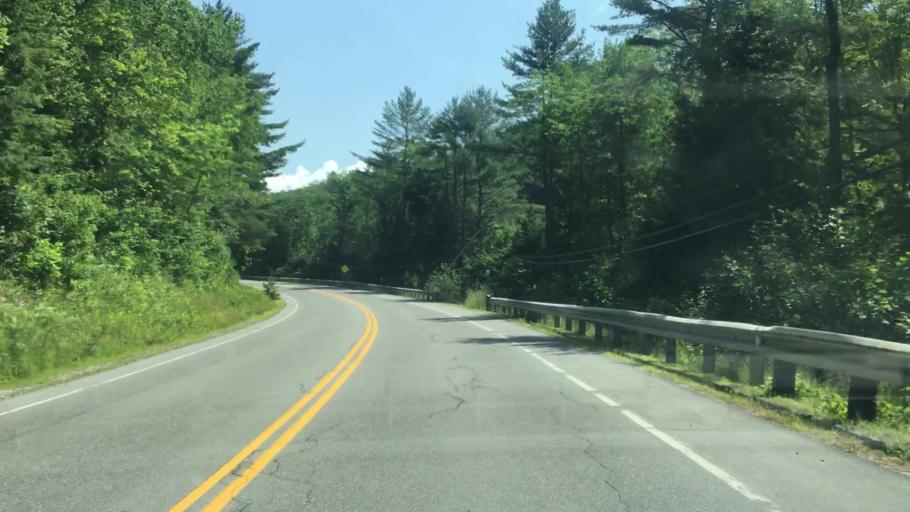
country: US
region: New Hampshire
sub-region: Sullivan County
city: Newport
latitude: 43.4158
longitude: -72.1811
